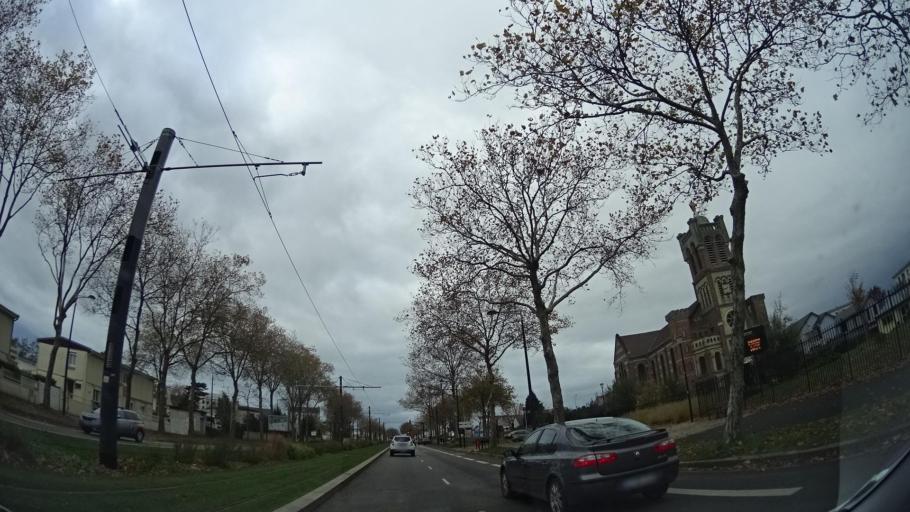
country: FR
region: Haute-Normandie
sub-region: Departement de la Seine-Maritime
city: Le Havre
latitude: 49.5140
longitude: 0.1239
